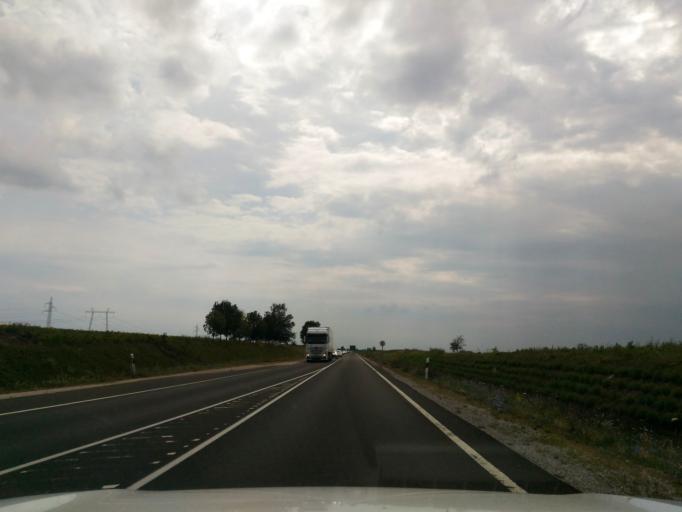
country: HU
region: Pest
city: Abony
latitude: 47.2193
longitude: 20.0212
